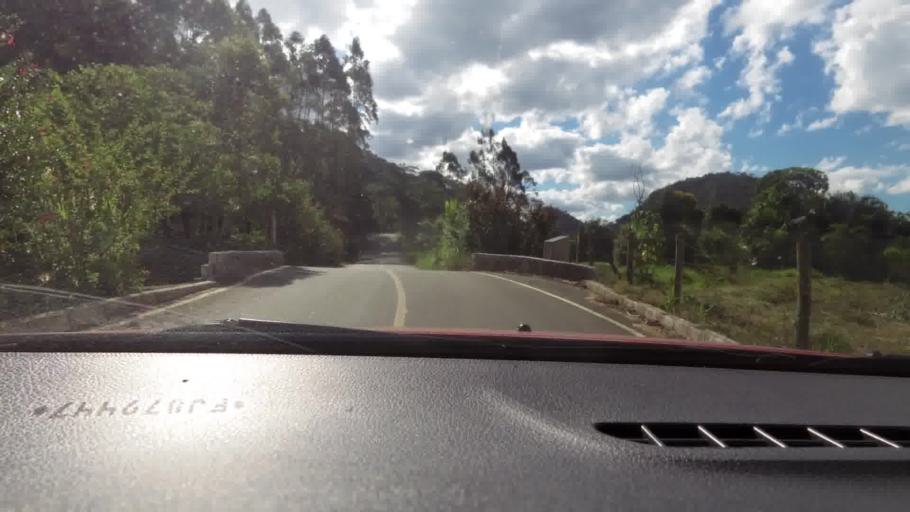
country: BR
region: Espirito Santo
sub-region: Guarapari
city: Guarapari
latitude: -20.5808
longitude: -40.5403
